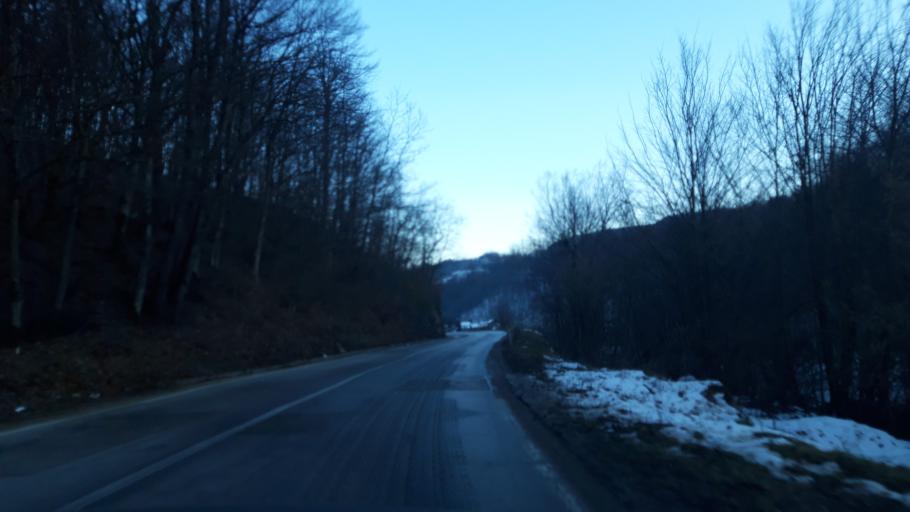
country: BA
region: Republika Srpska
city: Milici
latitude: 44.1653
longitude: 19.0406
